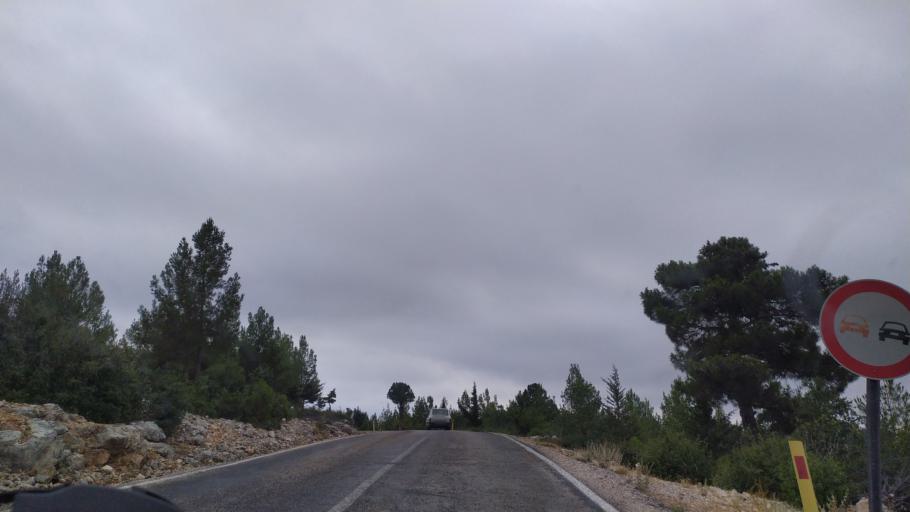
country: TR
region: Mersin
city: Silifke
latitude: 36.5445
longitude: 33.9266
